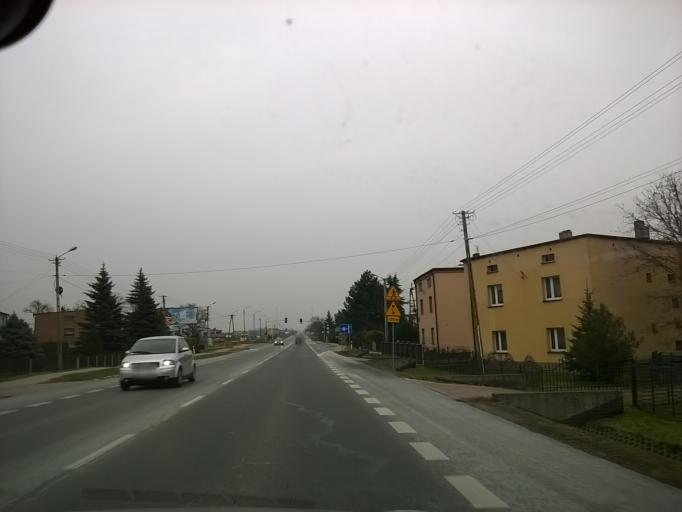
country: PL
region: Silesian Voivodeship
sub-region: Powiat gliwicki
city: Paniowki
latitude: 50.2401
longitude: 18.7683
